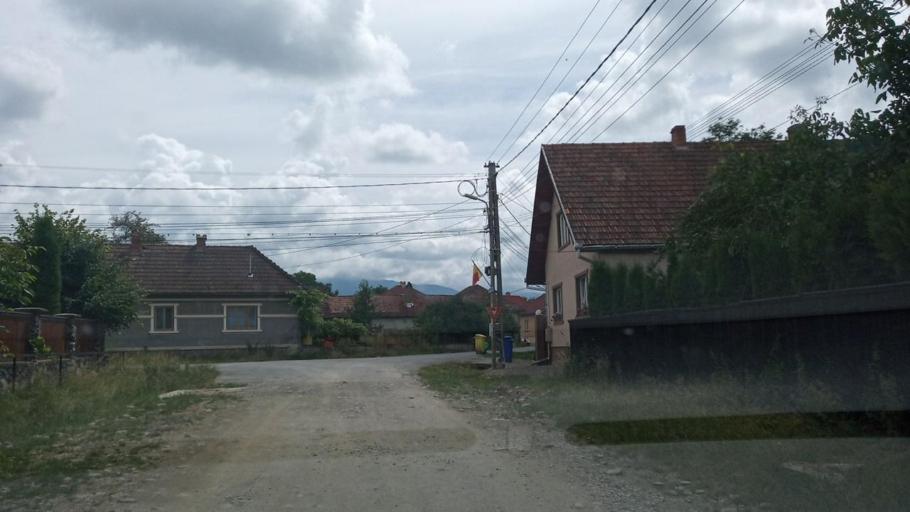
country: RO
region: Sibiu
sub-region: Comuna Cartisoara
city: Cartisoara
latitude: 45.7280
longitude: 24.5839
